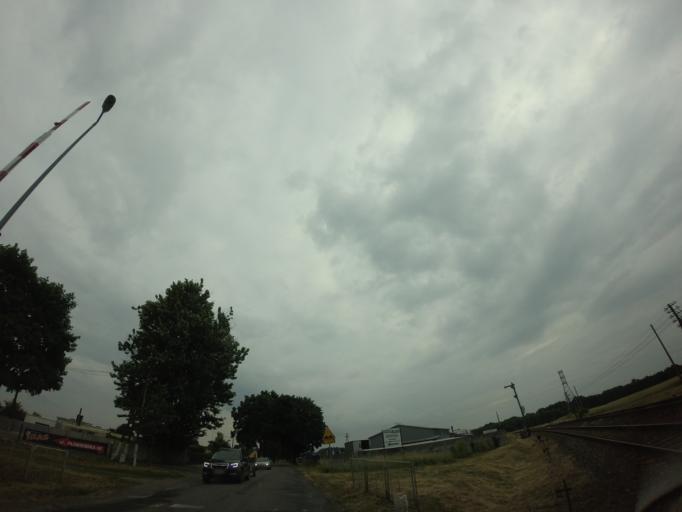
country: PL
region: West Pomeranian Voivodeship
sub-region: Powiat drawski
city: Czaplinek
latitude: 53.5354
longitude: 16.2312
